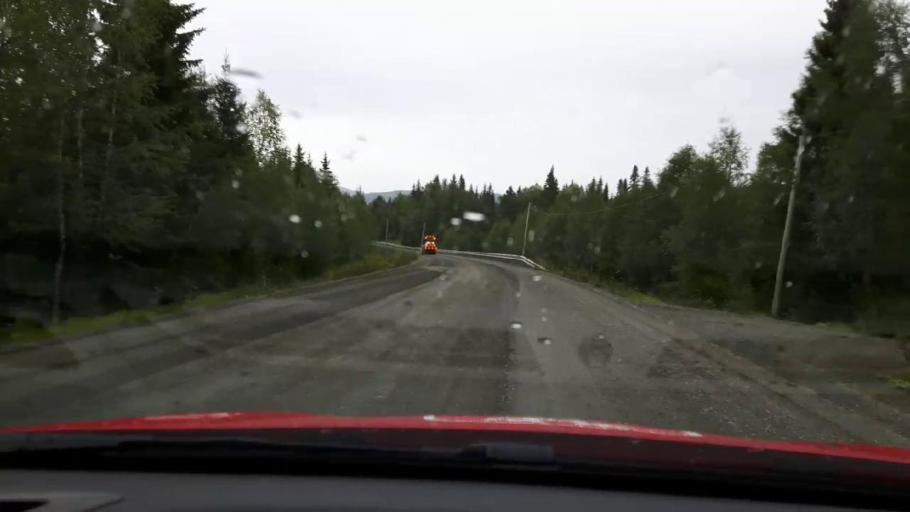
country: SE
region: Jaemtland
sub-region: Are Kommun
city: Are
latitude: 63.4068
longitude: 12.8012
